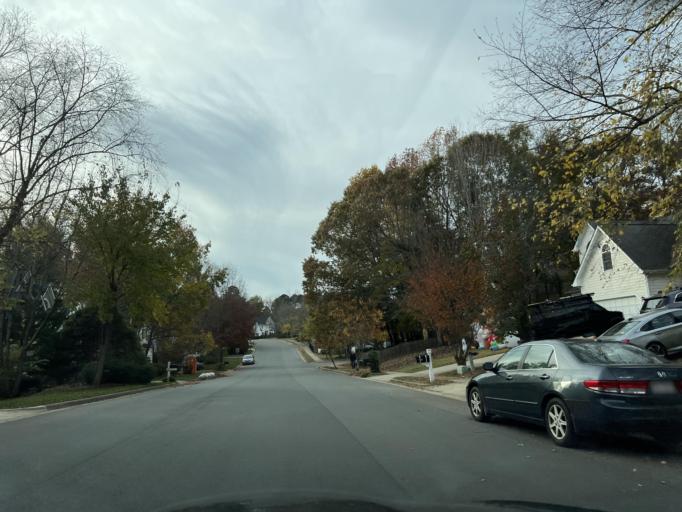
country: US
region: North Carolina
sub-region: Wake County
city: Wake Forest
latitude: 35.8929
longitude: -78.5912
